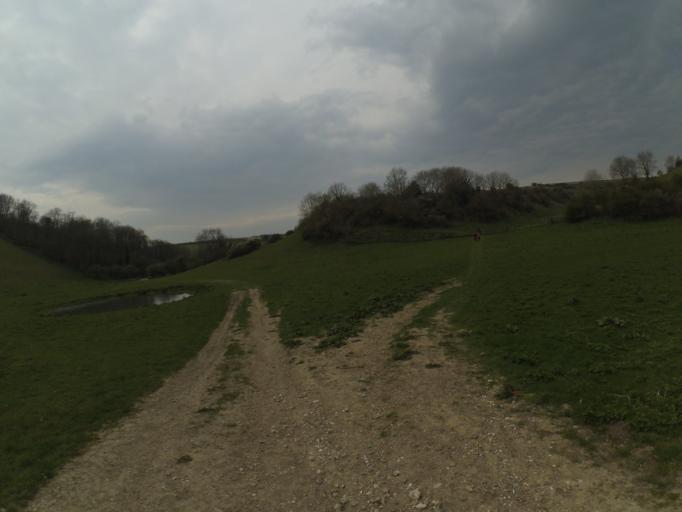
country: GB
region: England
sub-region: West Sussex
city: Arundel
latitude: 50.8943
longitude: -0.5207
